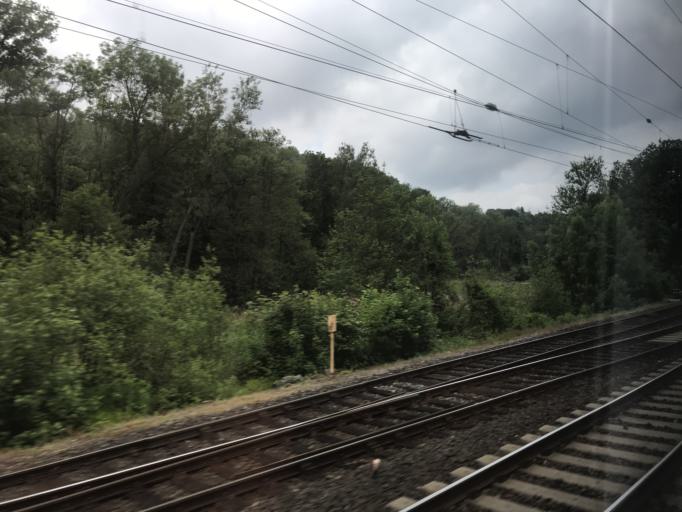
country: DE
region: Bavaria
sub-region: Swabia
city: Offingen
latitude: 48.4792
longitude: 10.3376
